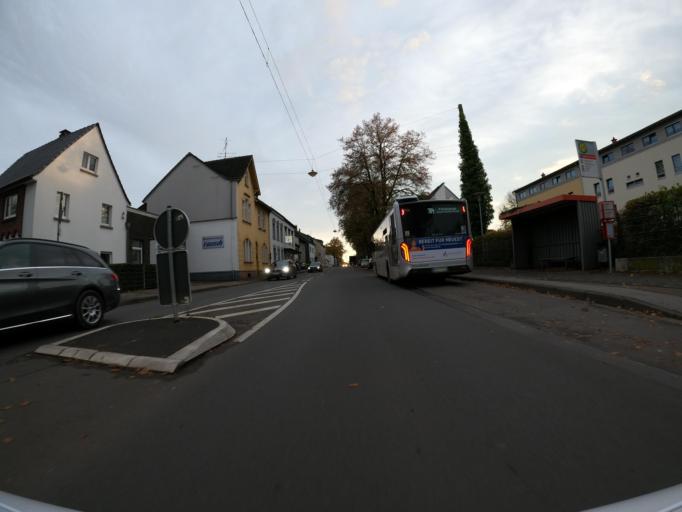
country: DE
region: North Rhine-Westphalia
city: Haan
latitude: 51.1988
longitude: 7.0162
